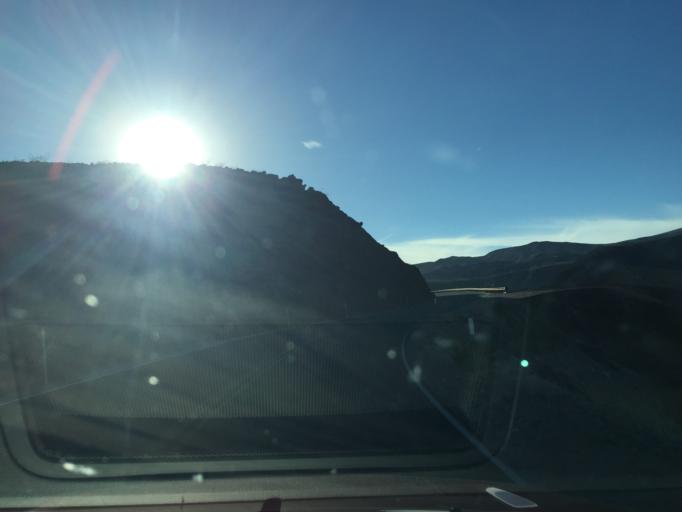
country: US
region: California
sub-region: San Bernardino County
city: Searles Valley
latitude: 36.3455
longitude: -117.5026
